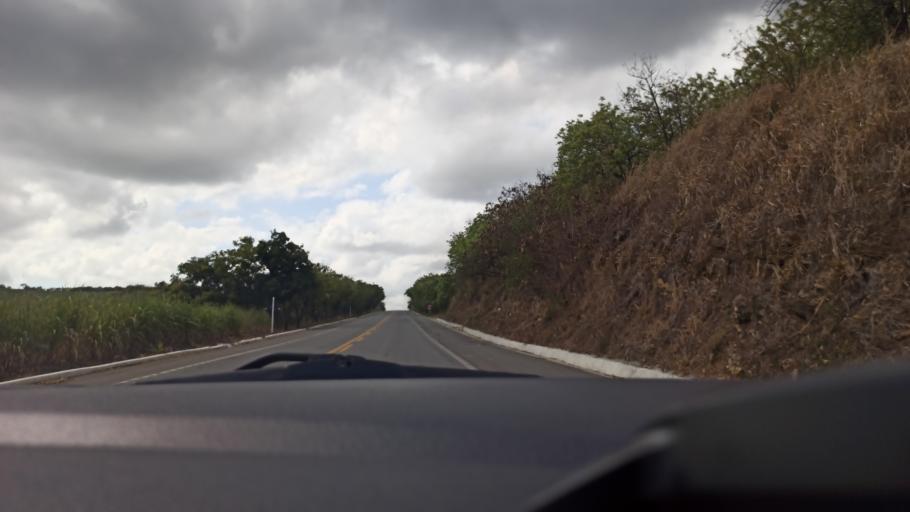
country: BR
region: Pernambuco
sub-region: Timbauba
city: Timbauba
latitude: -7.5312
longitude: -35.2897
